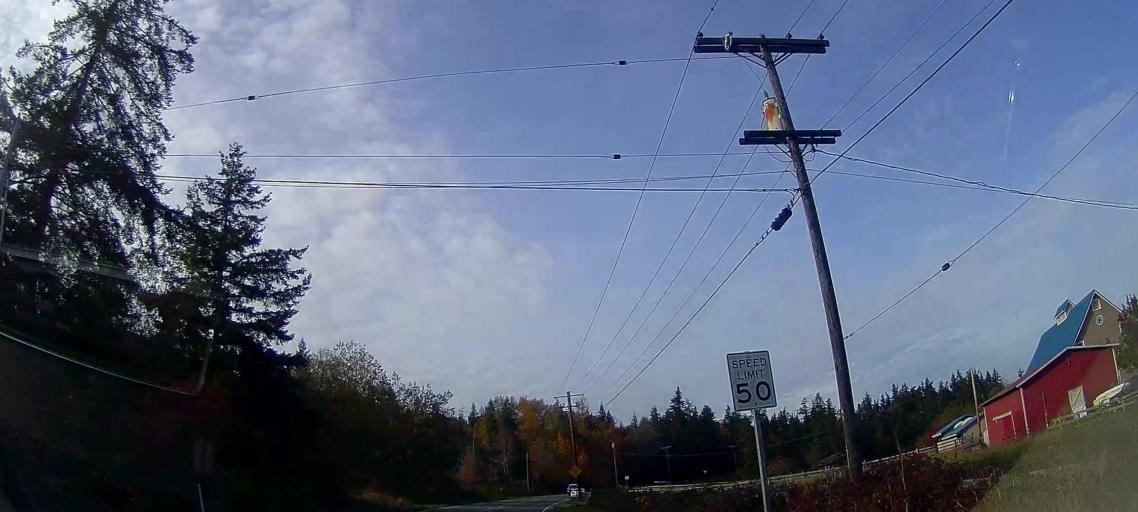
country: US
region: Washington
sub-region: Snohomish County
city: Stanwood
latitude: 48.2431
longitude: -122.4581
